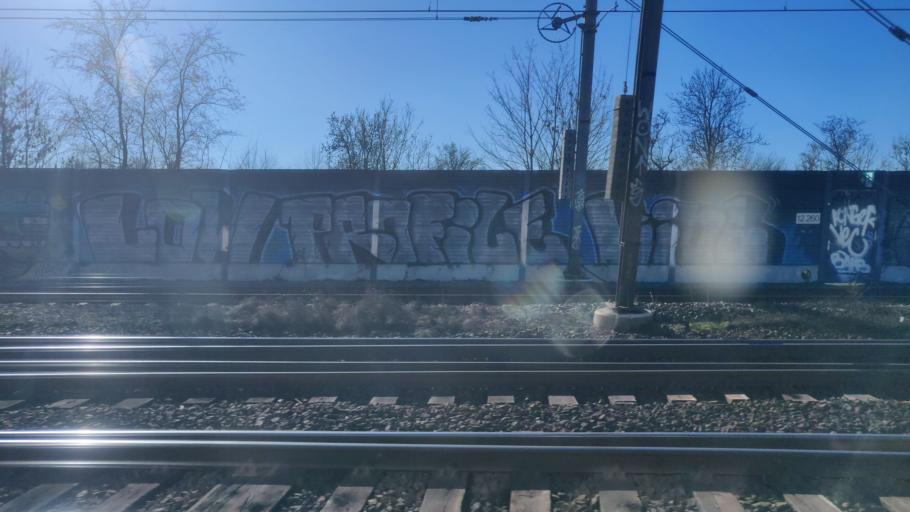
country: NL
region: North Holland
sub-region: Gemeente Weesp
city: Weesp
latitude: 52.3171
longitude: 5.0348
